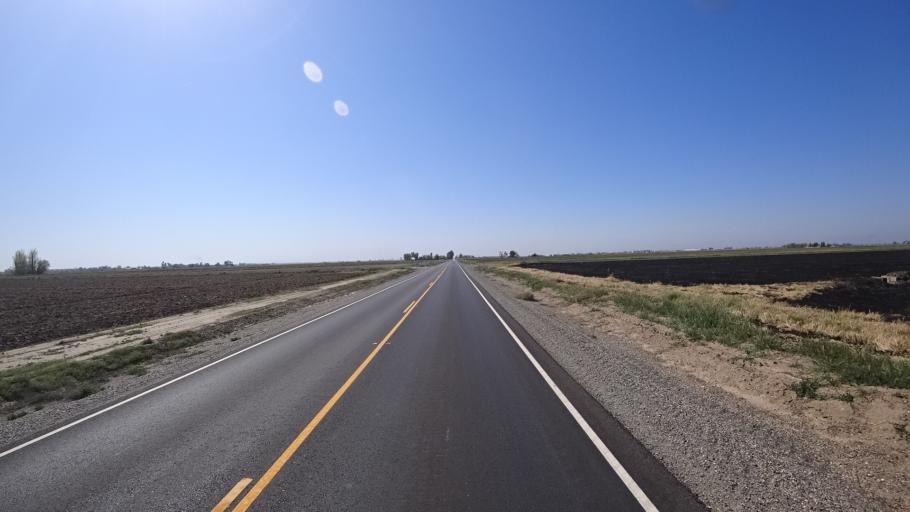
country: US
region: California
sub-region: Glenn County
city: Willows
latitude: 39.5953
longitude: -122.0651
